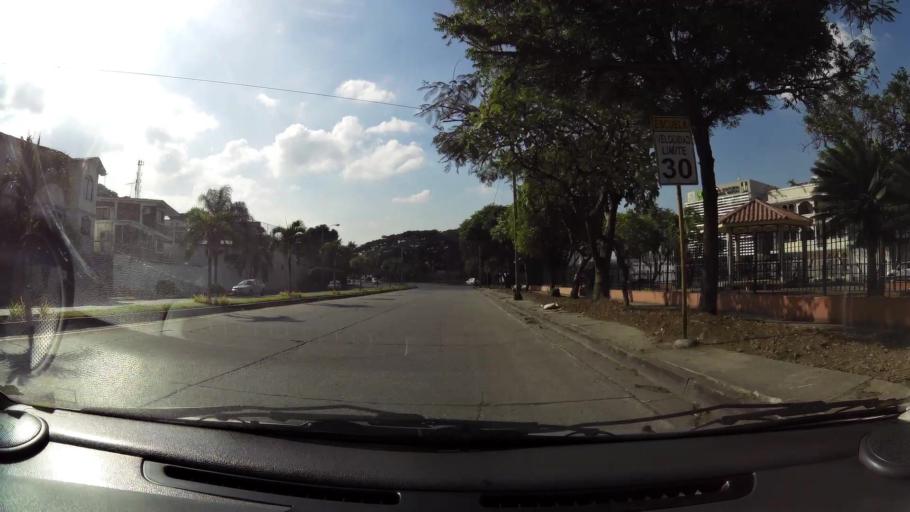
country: EC
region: Guayas
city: Guayaquil
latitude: -2.1653
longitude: -79.9454
